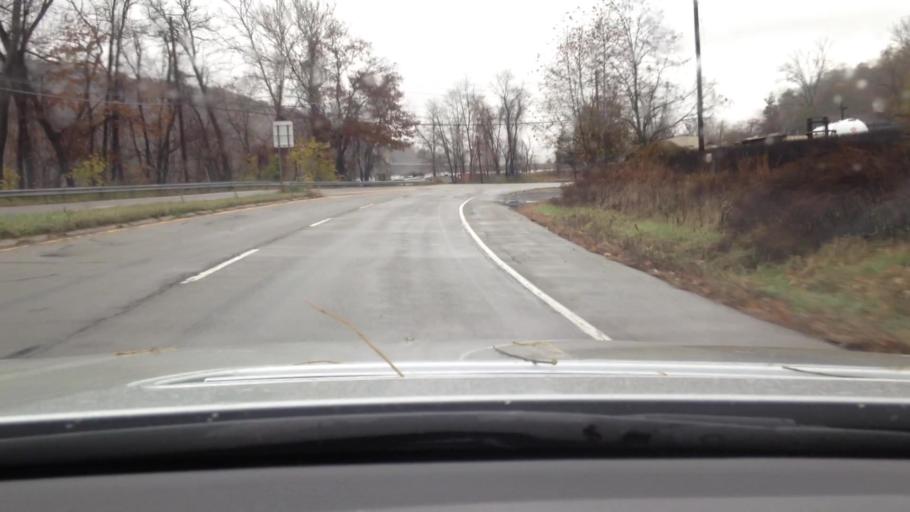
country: US
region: New York
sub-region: Westchester County
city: Peekskill
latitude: 41.3044
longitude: -73.9298
